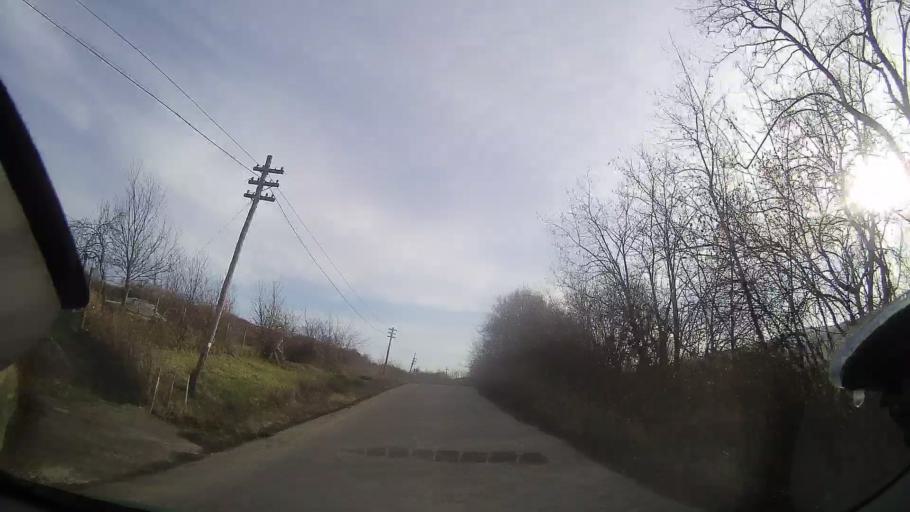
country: RO
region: Bihor
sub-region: Comuna Sarbi
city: Sarbi
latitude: 47.1885
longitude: 22.1261
